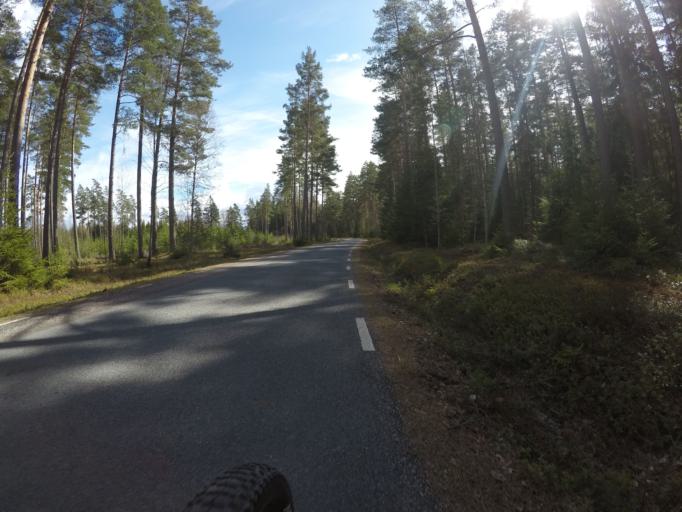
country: SE
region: Vaestmanland
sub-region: Kungsors Kommun
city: Kungsoer
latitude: 59.3167
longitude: 16.1164
